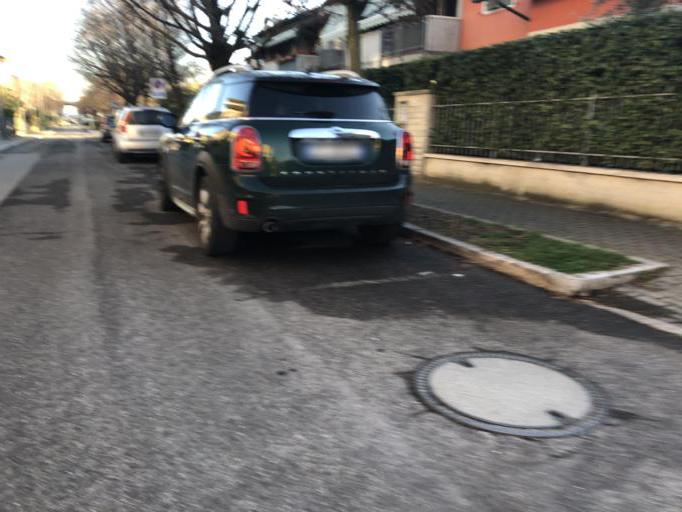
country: IT
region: Veneto
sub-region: Provincia di Verona
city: Caselle
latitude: 45.4157
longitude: 10.9026
